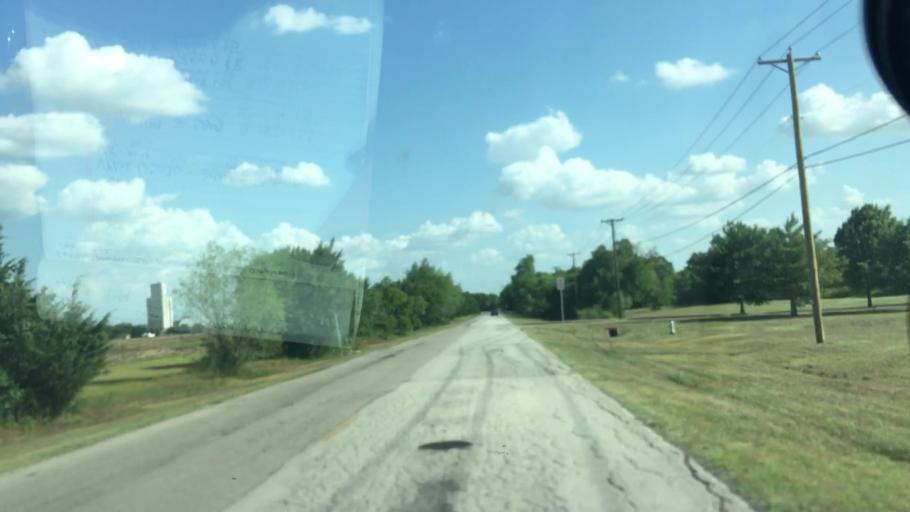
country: US
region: Texas
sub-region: Dallas County
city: Lancaster
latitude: 32.6107
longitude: -96.7535
